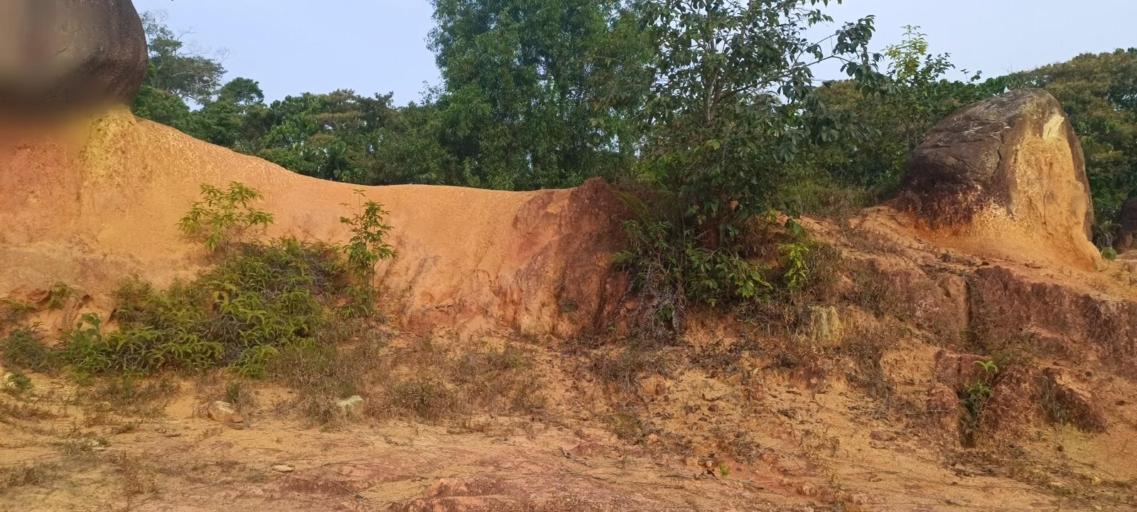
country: MY
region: Penang
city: Juru
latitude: 5.2730
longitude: 100.4196
